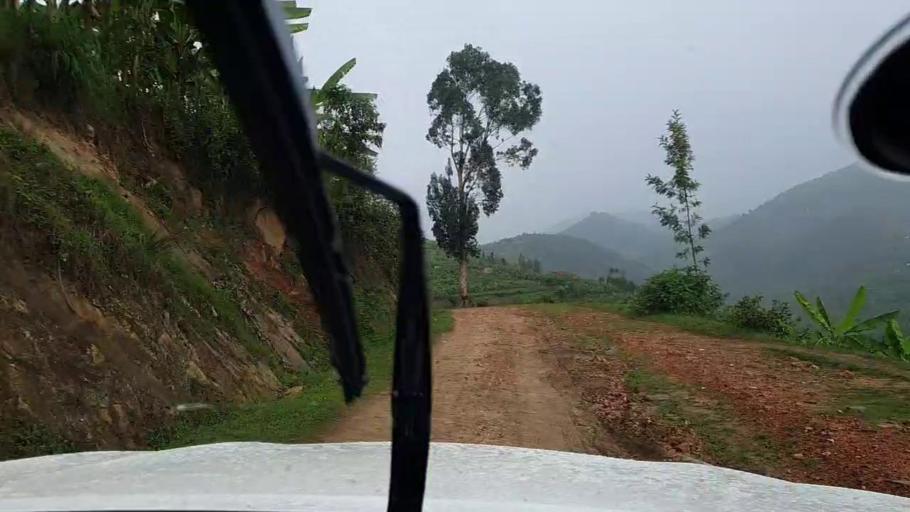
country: RW
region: Western Province
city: Kibuye
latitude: -2.0783
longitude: 29.4486
